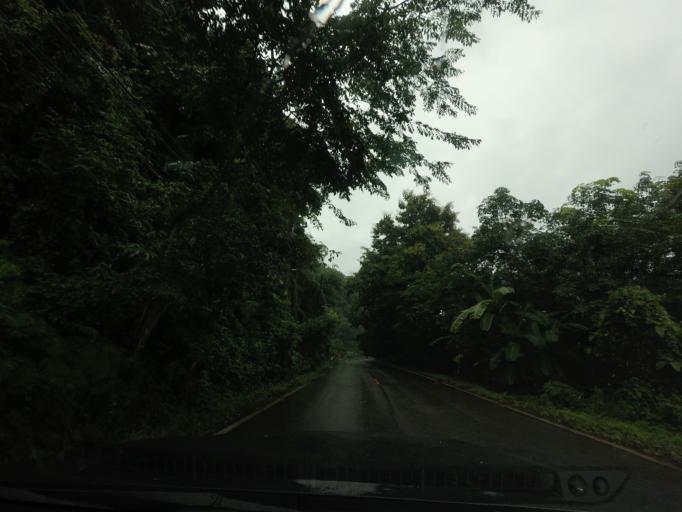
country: TH
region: Nong Khai
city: Sangkhom
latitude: 18.2031
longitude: 102.1558
